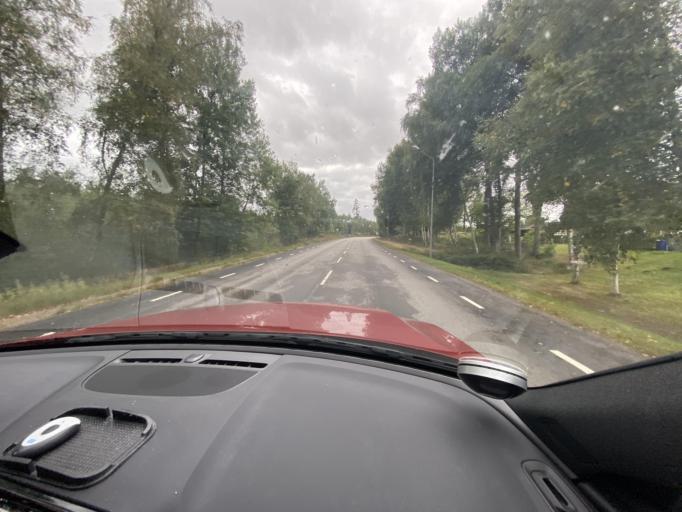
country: SE
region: Kronoberg
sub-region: Markaryds Kommun
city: Markaryd
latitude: 56.4596
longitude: 13.6189
